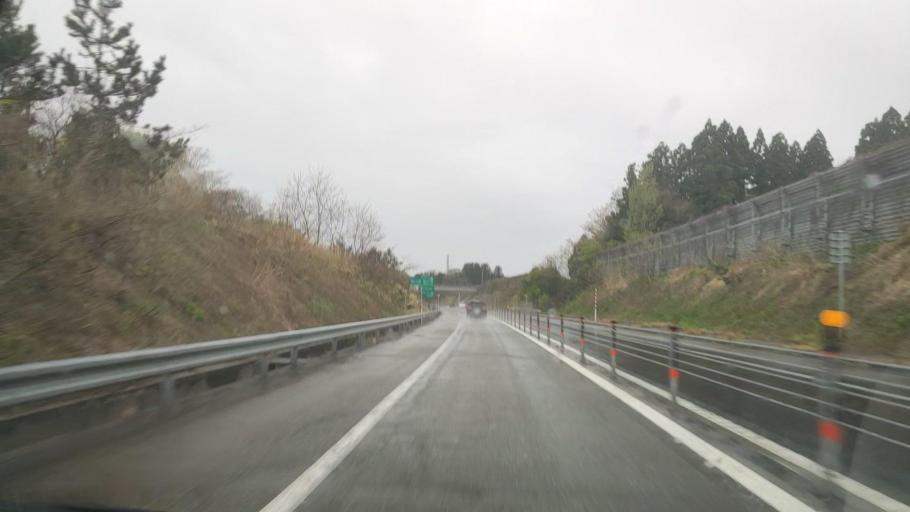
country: JP
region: Akita
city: Noshiromachi
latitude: 40.1595
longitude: 140.0298
